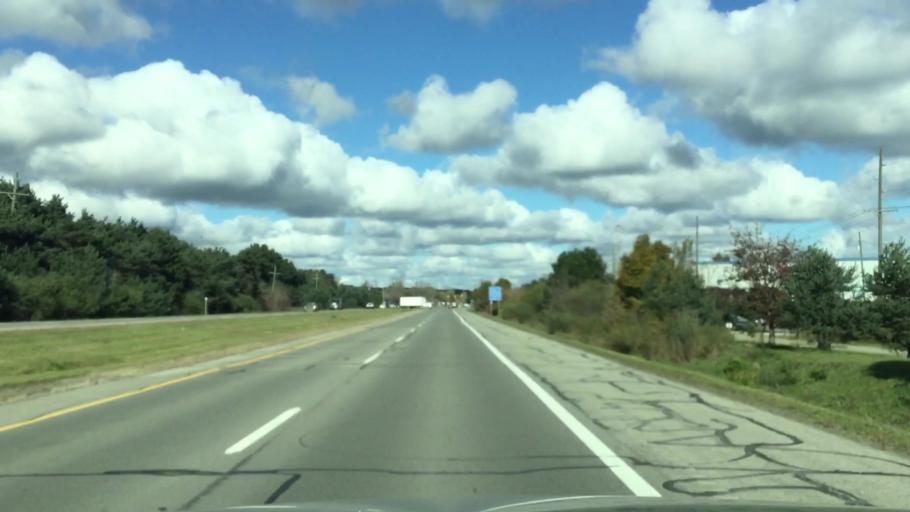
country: US
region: Michigan
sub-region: Oakland County
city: Oxford
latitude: 42.8650
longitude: -83.2925
